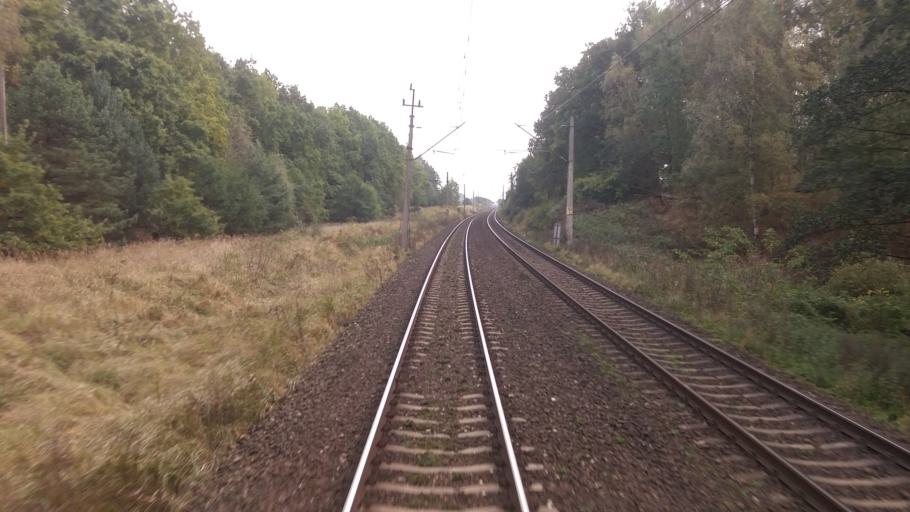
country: PL
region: West Pomeranian Voivodeship
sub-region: Powiat stargardzki
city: Dolice
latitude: 53.2061
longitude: 15.1830
